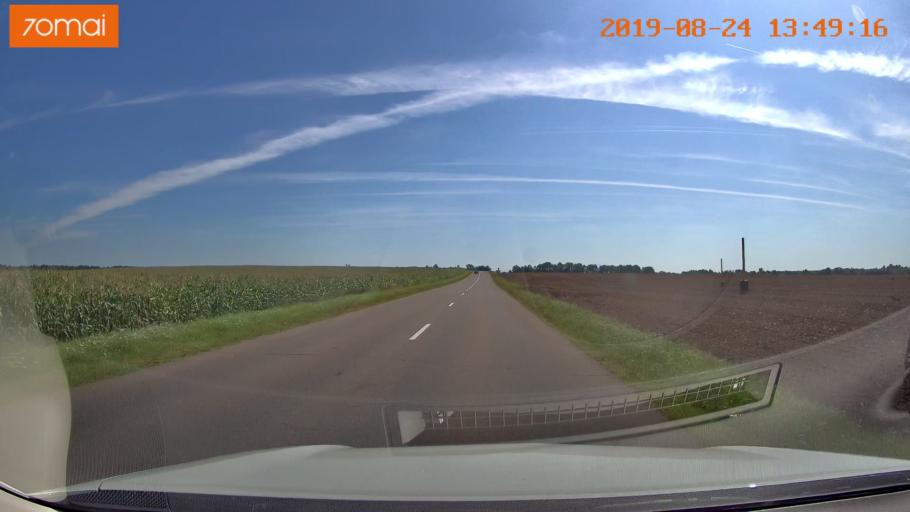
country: BY
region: Minsk
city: Samakhvalavichy
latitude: 53.6372
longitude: 27.5559
